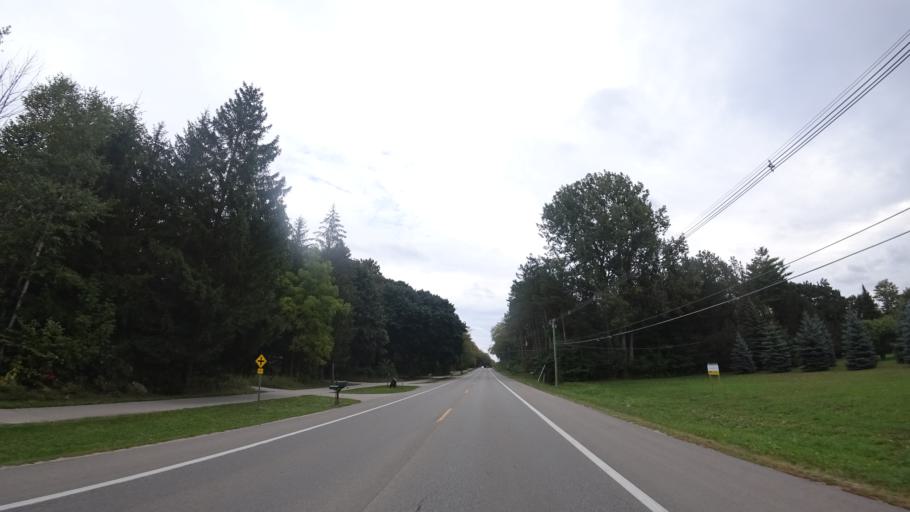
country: US
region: Michigan
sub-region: Emmet County
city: Harbor Springs
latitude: 45.4308
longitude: -84.9317
